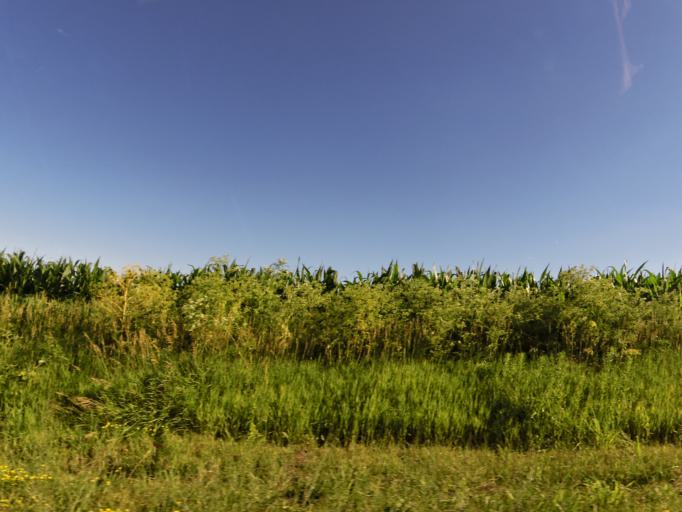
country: US
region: Missouri
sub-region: Marion County
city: Hannibal
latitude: 39.7035
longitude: -91.4338
